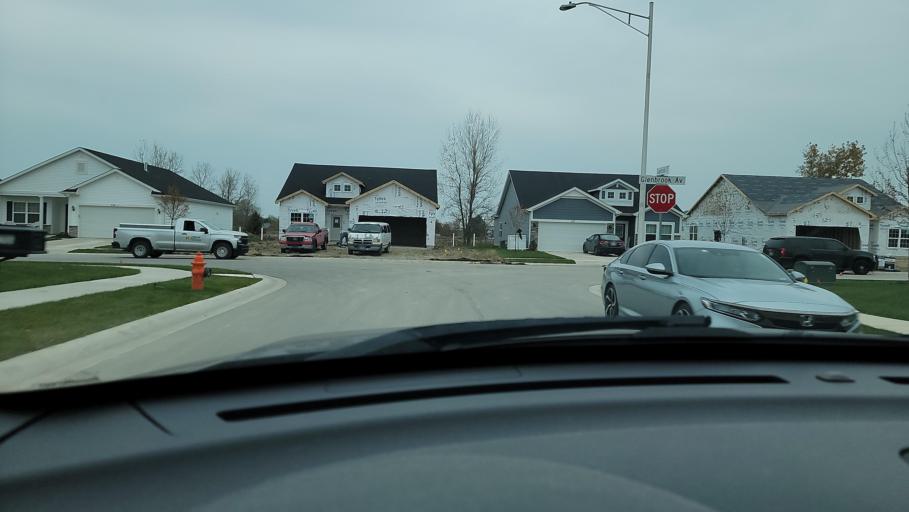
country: US
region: Indiana
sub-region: Porter County
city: Portage
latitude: 41.5463
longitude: -87.1697
